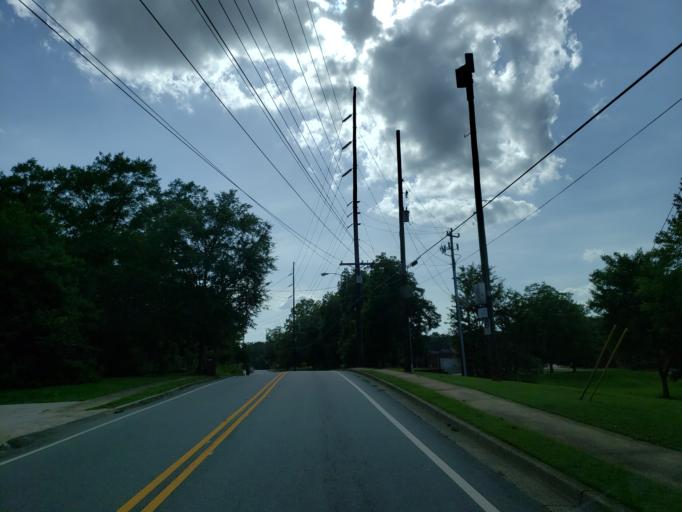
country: US
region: Georgia
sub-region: Cobb County
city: Powder Springs
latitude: 33.8753
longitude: -84.6657
